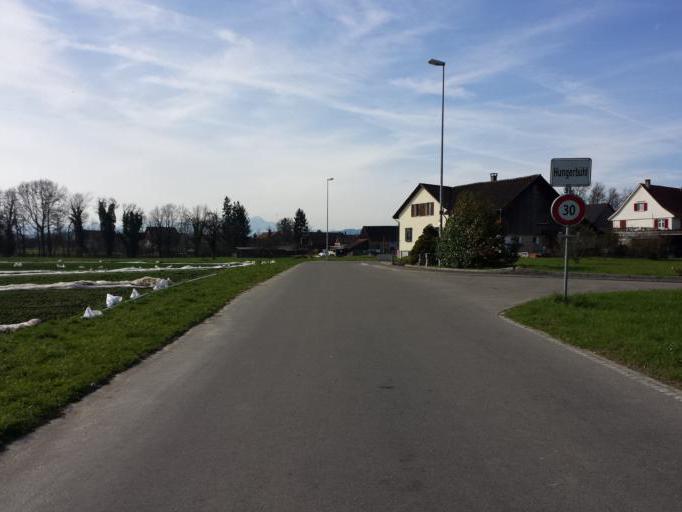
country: CH
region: Thurgau
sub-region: Arbon District
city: Salmsach
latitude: 47.5530
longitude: 9.3578
